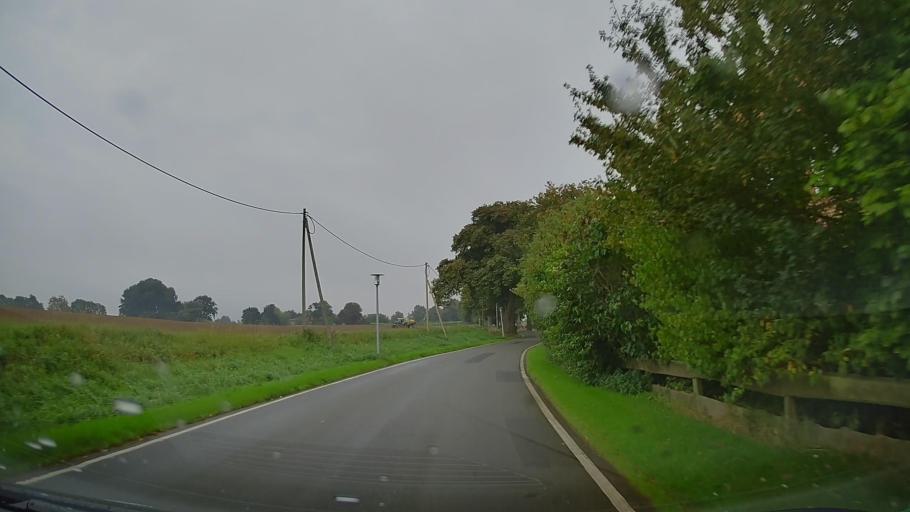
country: DE
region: Mecklenburg-Vorpommern
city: Kalkhorst
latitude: 53.9972
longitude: 11.0984
